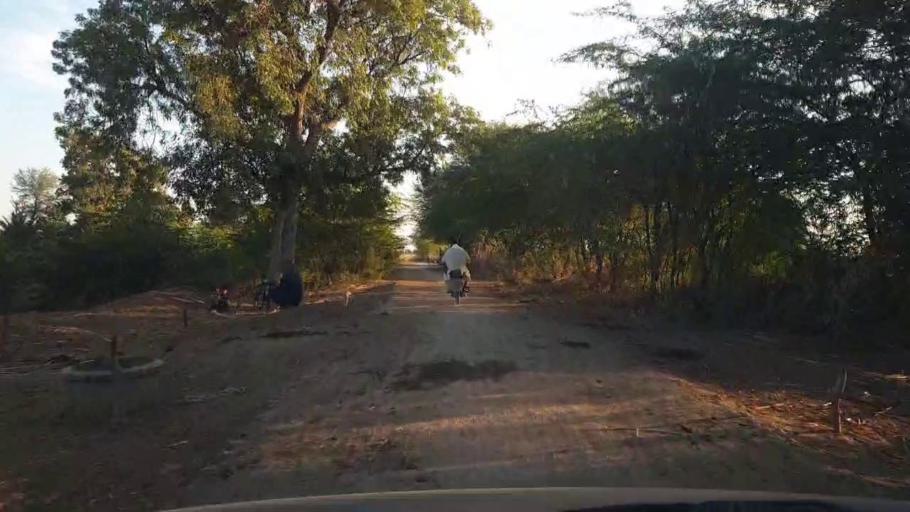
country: PK
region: Sindh
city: Dhoro Naro
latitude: 25.3612
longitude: 69.5652
